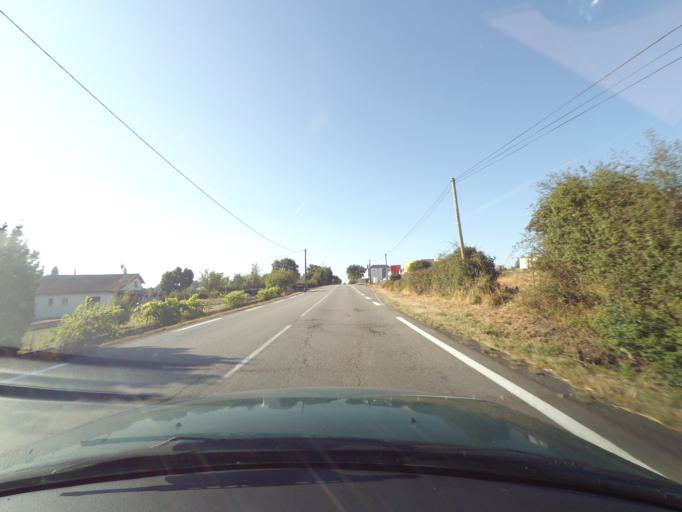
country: FR
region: Poitou-Charentes
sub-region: Departement des Deux-Sevres
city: Chiche
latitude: 46.7543
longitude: -0.3088
